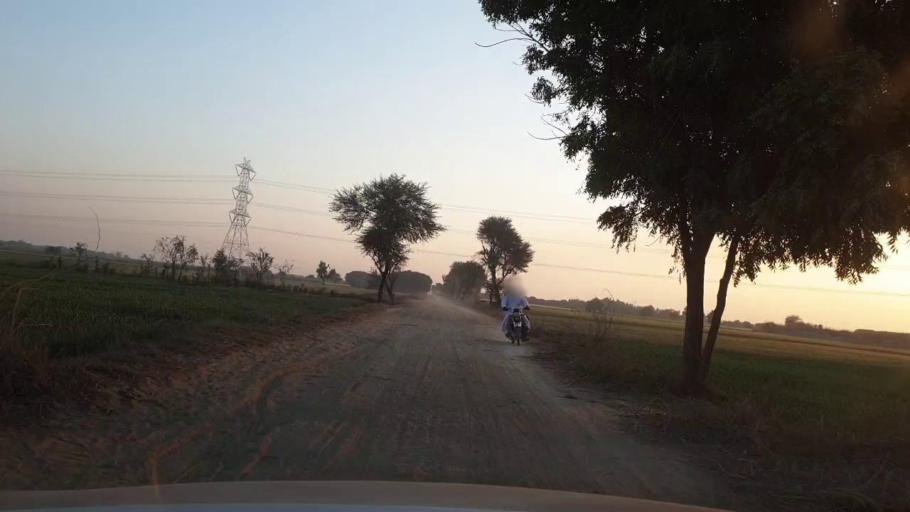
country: PK
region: Sindh
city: Tando Allahyar
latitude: 25.5392
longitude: 68.6290
